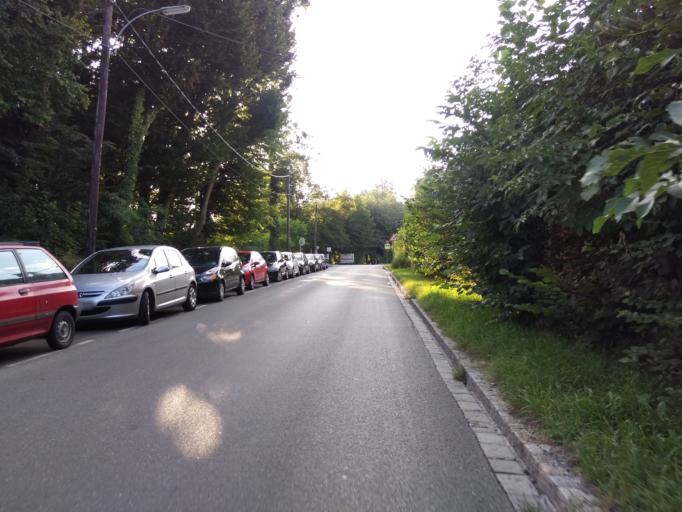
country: AT
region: Styria
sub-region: Graz Stadt
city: Graz
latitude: 47.0856
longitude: 15.4536
